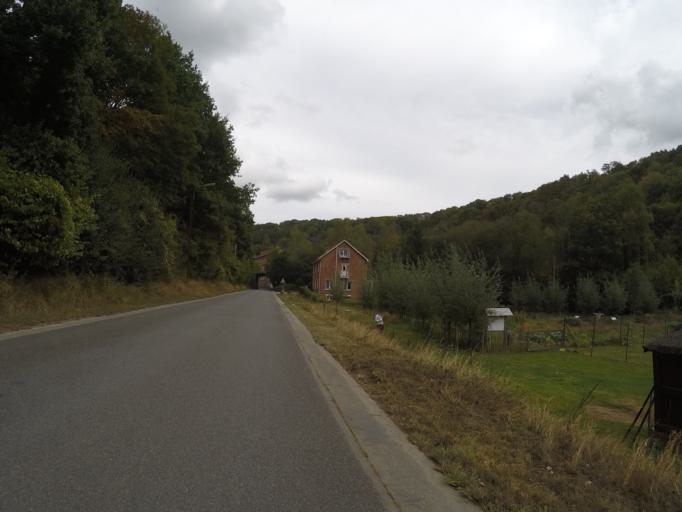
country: BE
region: Wallonia
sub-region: Province de Namur
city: Yvoir
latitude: 50.3370
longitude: 4.9030
